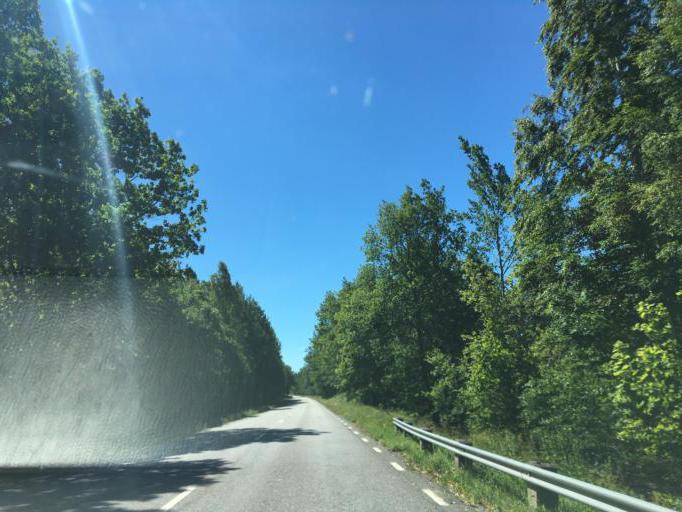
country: SE
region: OErebro
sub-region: Laxa Kommun
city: Laxa
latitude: 58.8376
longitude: 14.5470
